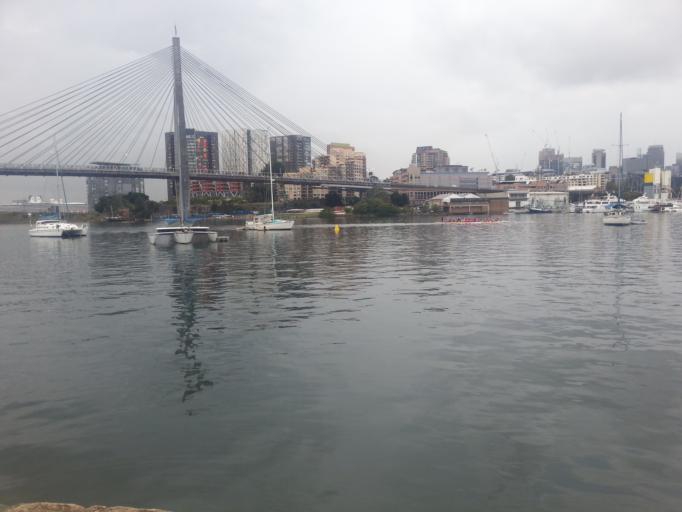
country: AU
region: New South Wales
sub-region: Leichhardt
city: Balmain East
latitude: -33.8729
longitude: 151.1860
